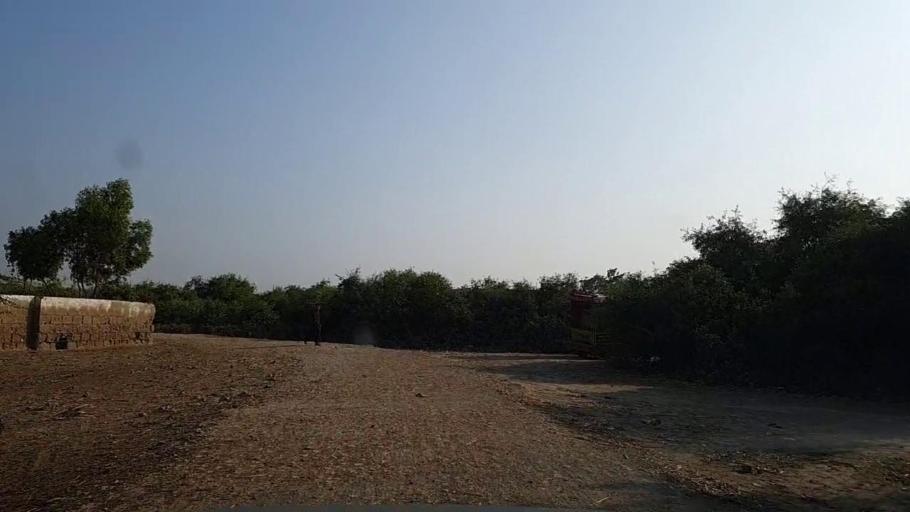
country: PK
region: Sindh
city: Mirpur Sakro
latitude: 24.5997
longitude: 67.6561
